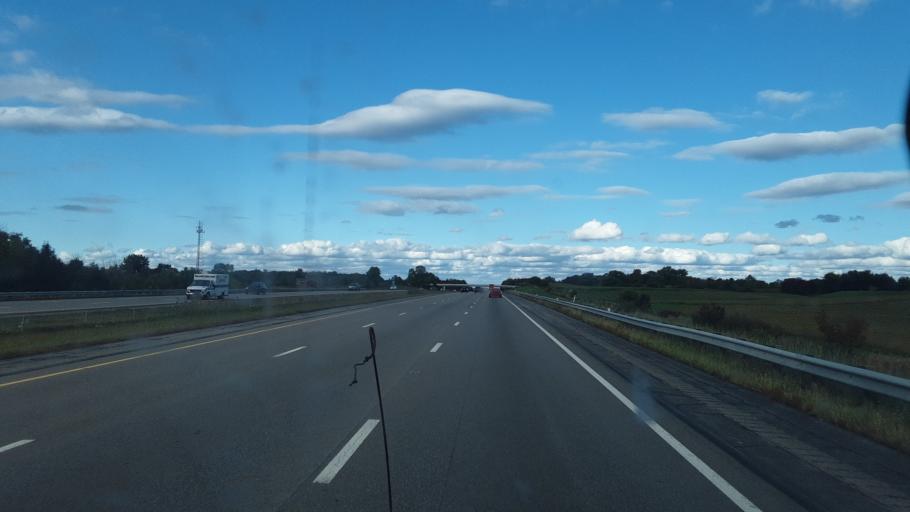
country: US
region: Ohio
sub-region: Medina County
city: Seville
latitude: 41.0731
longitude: -81.8447
